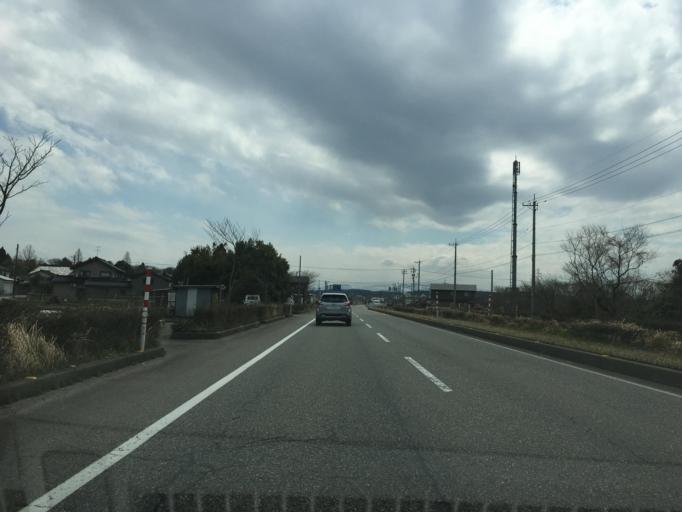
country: JP
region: Toyama
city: Kuragaki-kosugi
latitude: 36.7052
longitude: 137.1153
